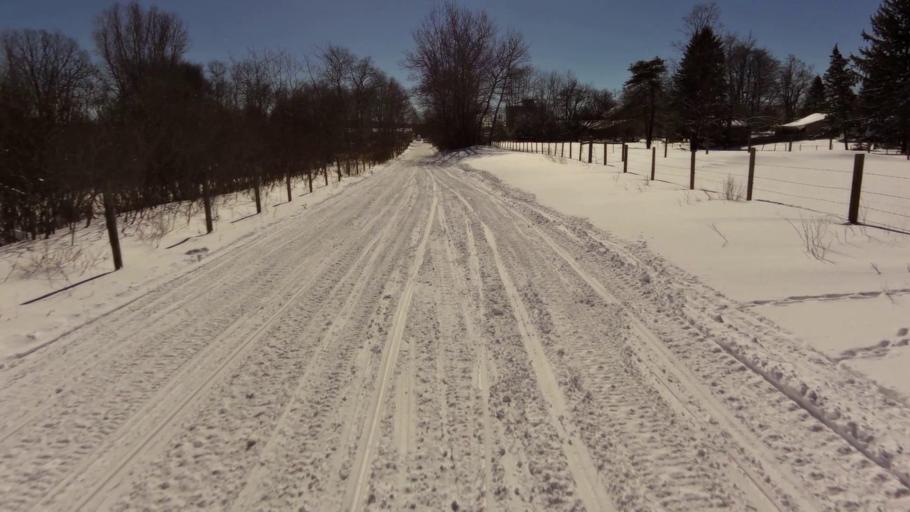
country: US
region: New York
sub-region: Chautauqua County
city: Mayville
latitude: 42.1669
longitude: -79.5839
